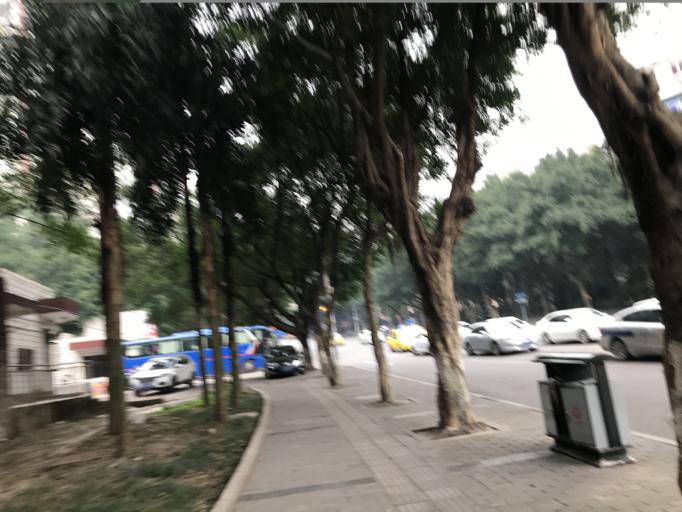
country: CN
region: Chongqing Shi
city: Chongqing
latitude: 29.5283
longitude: 106.5509
